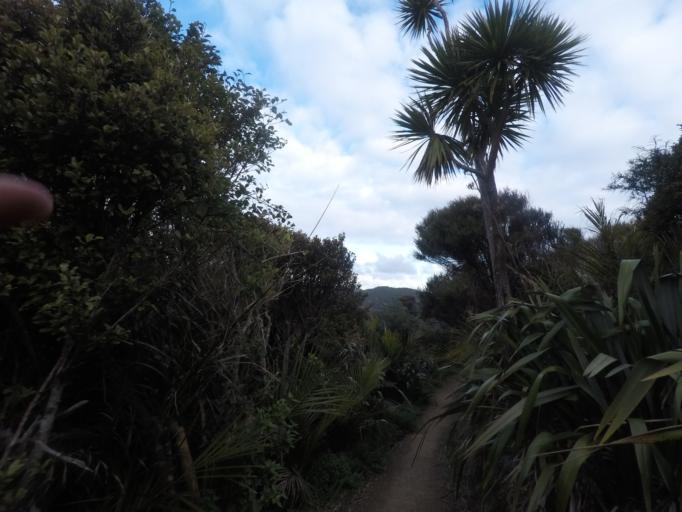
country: NZ
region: Auckland
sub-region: Auckland
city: Muriwai Beach
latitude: -36.9818
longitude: 174.4715
